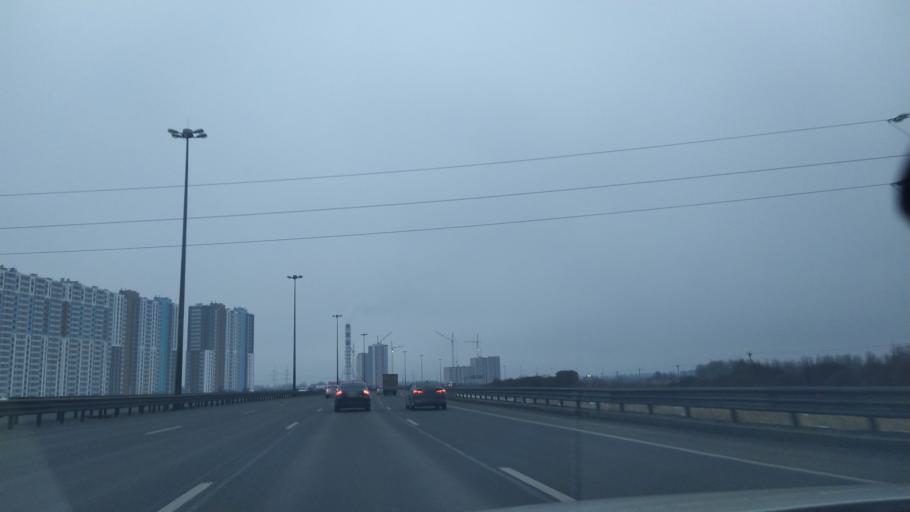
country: RU
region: St.-Petersburg
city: Krasnogvargeisky
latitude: 60.0123
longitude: 30.4720
